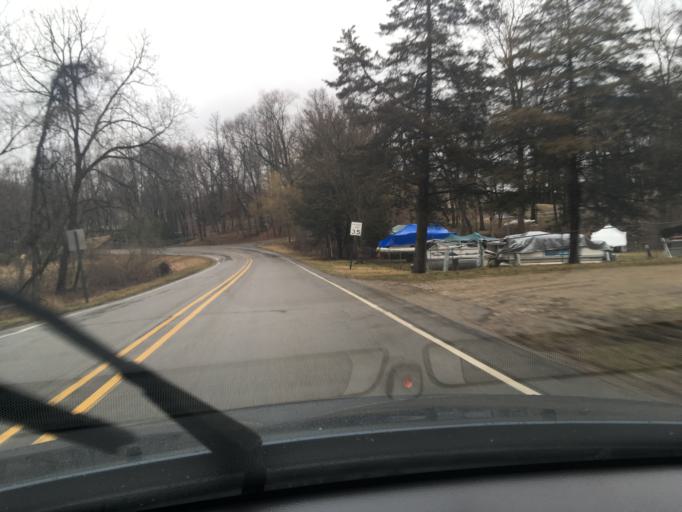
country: US
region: Michigan
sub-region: Jackson County
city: Grass Lake
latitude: 42.3293
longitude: -84.1554
